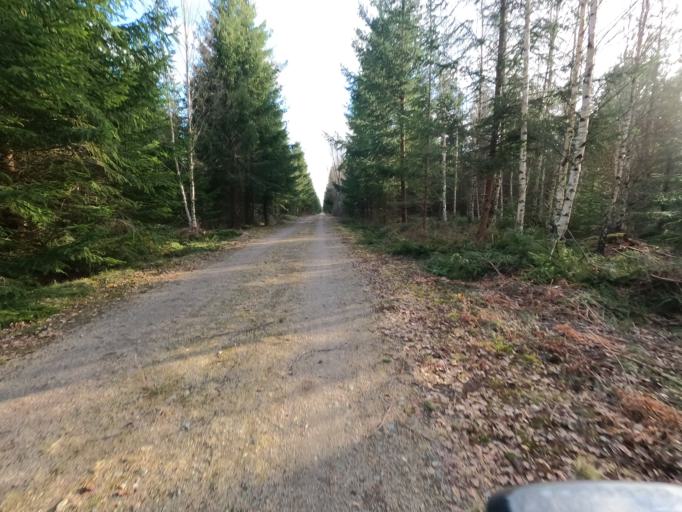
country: SE
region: Kronoberg
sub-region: Alvesta Kommun
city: Vislanda
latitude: 56.6493
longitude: 14.6176
